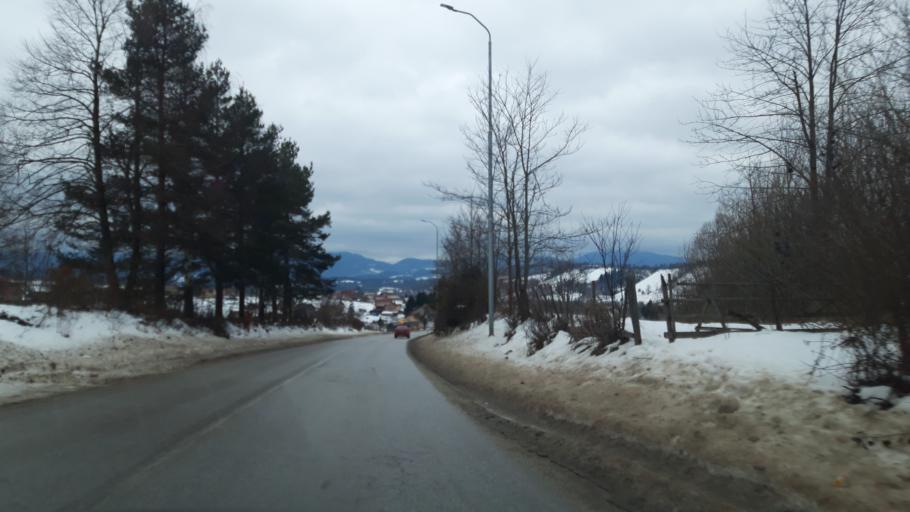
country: BA
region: Republika Srpska
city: Pale
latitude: 43.8893
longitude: 18.6170
